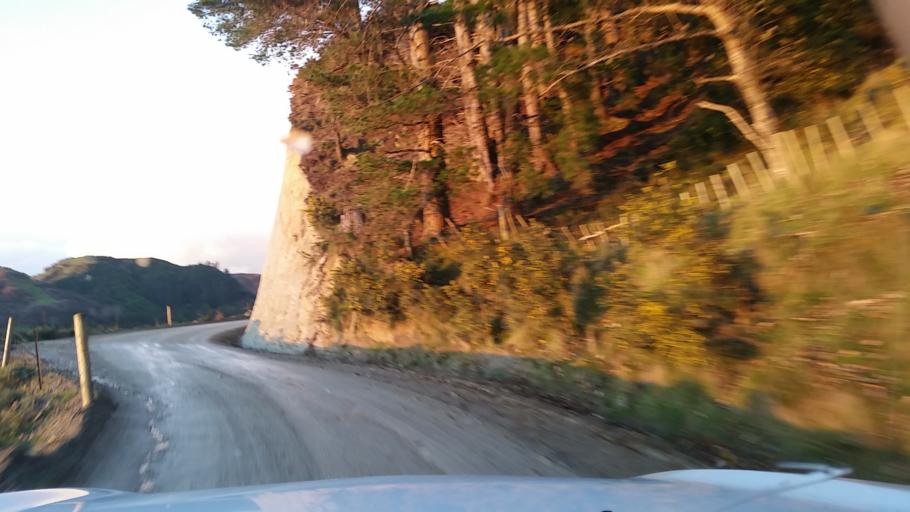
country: NZ
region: Manawatu-Wanganui
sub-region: Wanganui District
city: Wanganui
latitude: -39.7635
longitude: 174.8764
